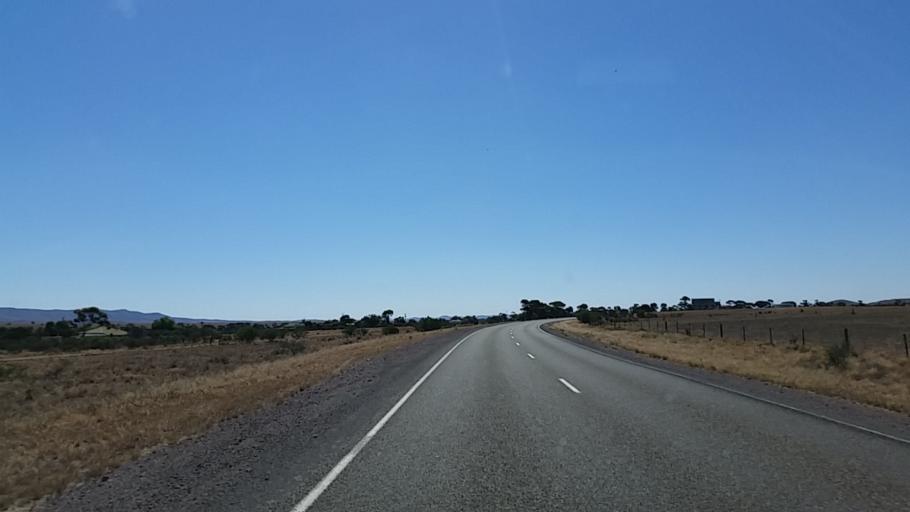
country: AU
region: South Australia
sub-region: Flinders Ranges
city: Quorn
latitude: -32.4320
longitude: 138.5323
